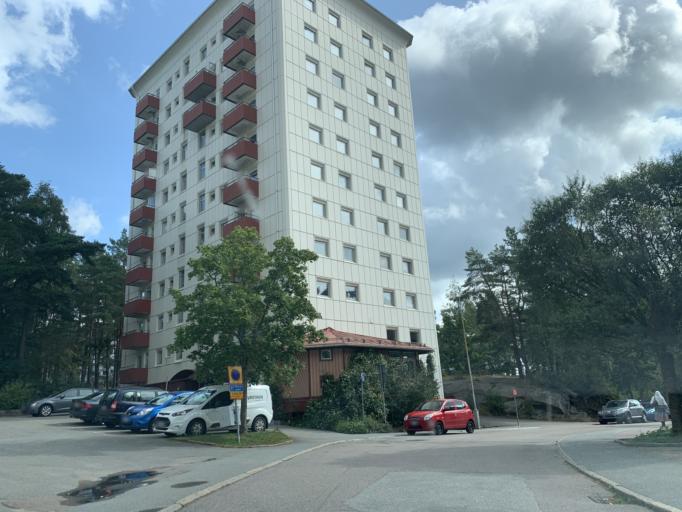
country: SE
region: Vaestra Goetaland
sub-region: Goteborg
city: Eriksbo
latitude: 57.7622
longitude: 12.0385
